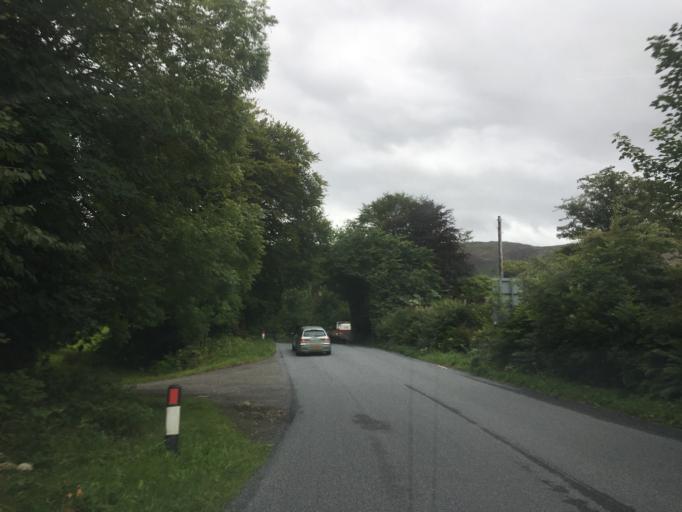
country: GB
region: Scotland
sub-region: Argyll and Bute
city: Oban
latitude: 56.2645
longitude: -5.4754
